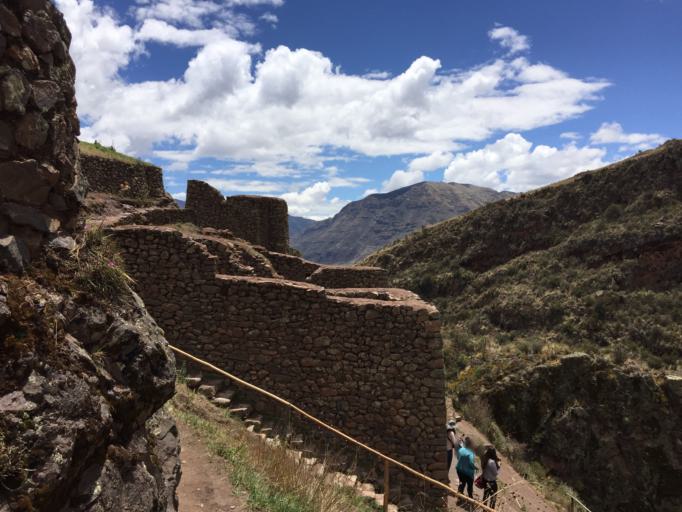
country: PE
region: Cusco
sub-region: Provincia de Calca
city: Pisac
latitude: -13.4080
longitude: -71.8446
